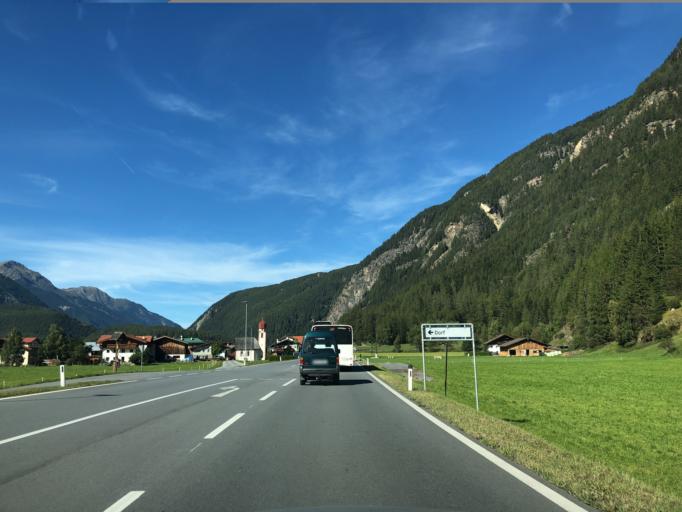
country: AT
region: Tyrol
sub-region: Politischer Bezirk Imst
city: Umhausen
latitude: 47.0873
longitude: 10.9605
